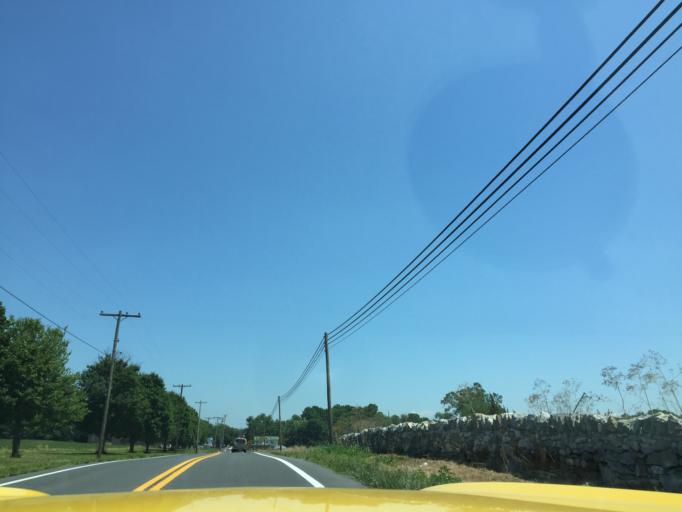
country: US
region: West Virginia
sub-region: Jefferson County
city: Charles Town
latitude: 39.2879
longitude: -77.8746
